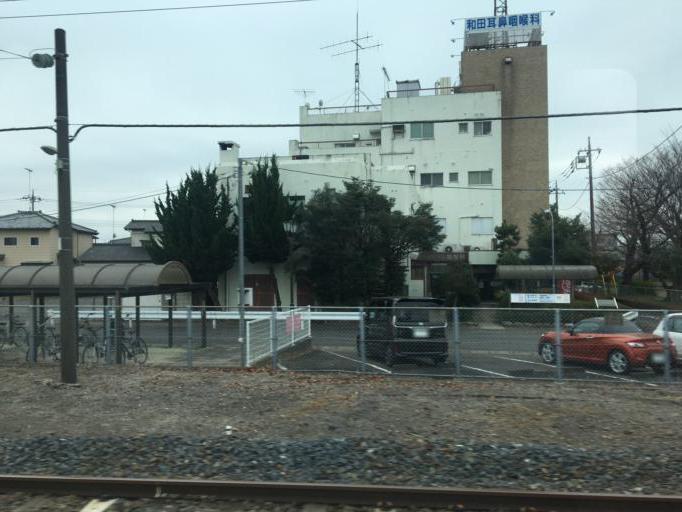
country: JP
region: Ibaraki
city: Yuki
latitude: 36.2984
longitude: 139.8707
